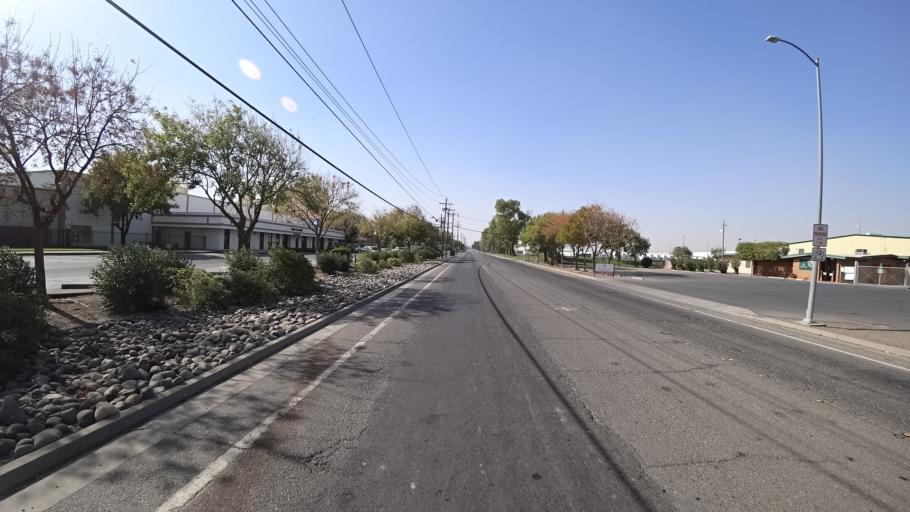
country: US
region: California
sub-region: Yolo County
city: Woodland
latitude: 38.6844
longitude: -121.7384
